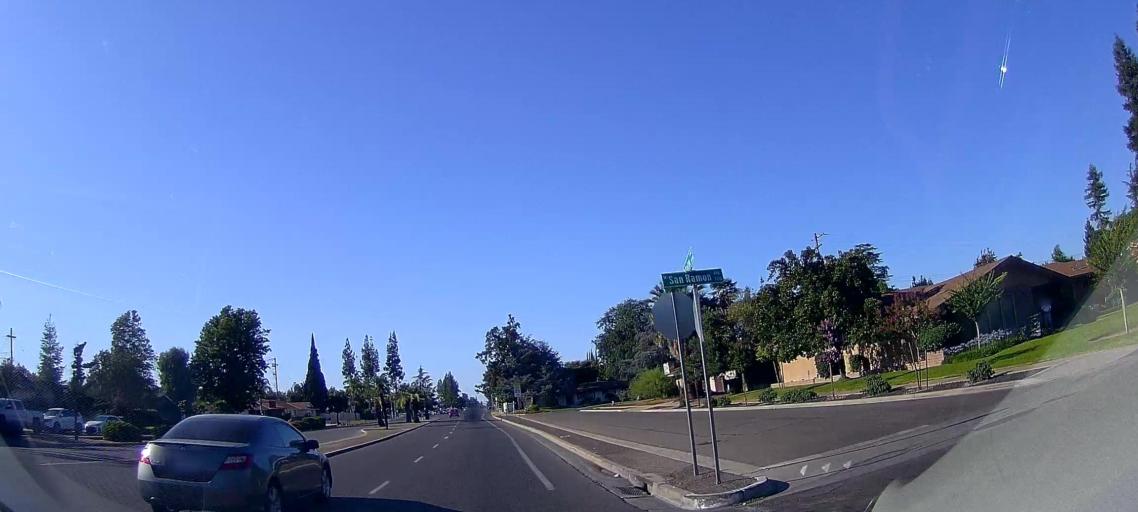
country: US
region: California
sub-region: Fresno County
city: Fresno
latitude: 36.8136
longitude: -119.8083
